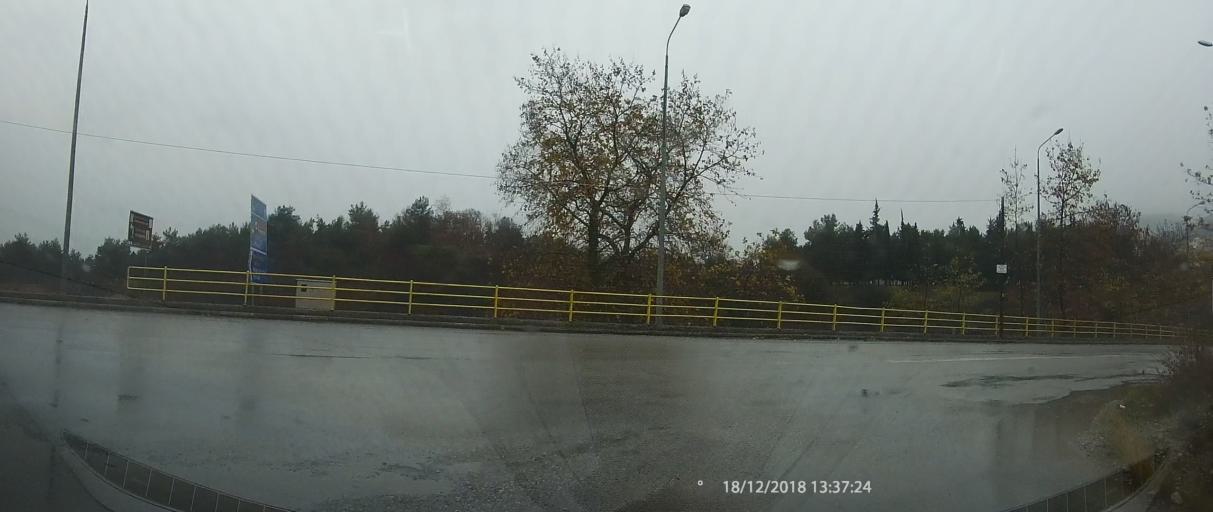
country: GR
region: Central Macedonia
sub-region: Nomos Pierias
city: Litochoro
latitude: 40.1082
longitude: 22.5035
